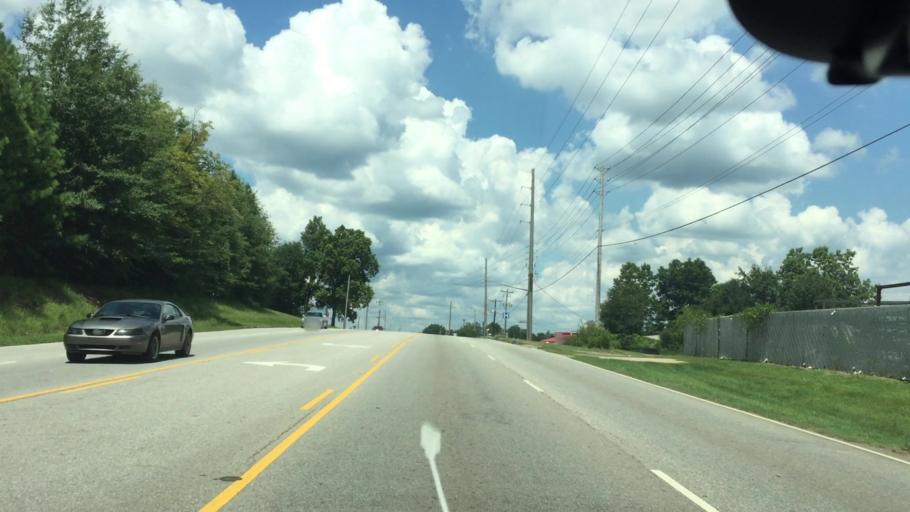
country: US
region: Alabama
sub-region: Pike County
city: Troy
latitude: 31.7894
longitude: -85.9792
